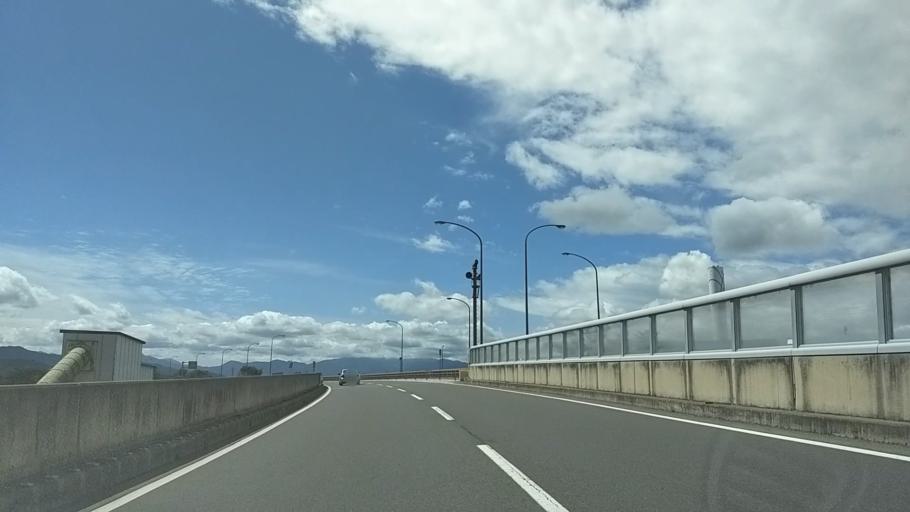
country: JP
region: Nagano
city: Nagano-shi
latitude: 36.6238
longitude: 138.2272
